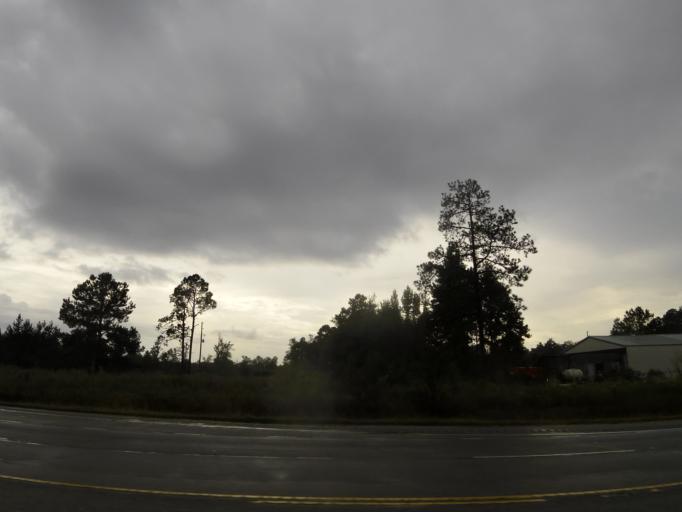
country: US
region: Georgia
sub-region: Wayne County
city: Jesup
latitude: 31.5894
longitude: -81.8637
